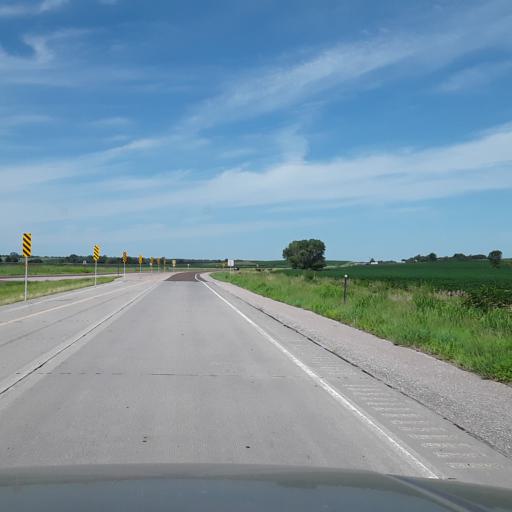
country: US
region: Nebraska
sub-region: Lancaster County
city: Lincoln
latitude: 40.8873
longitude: -96.8053
